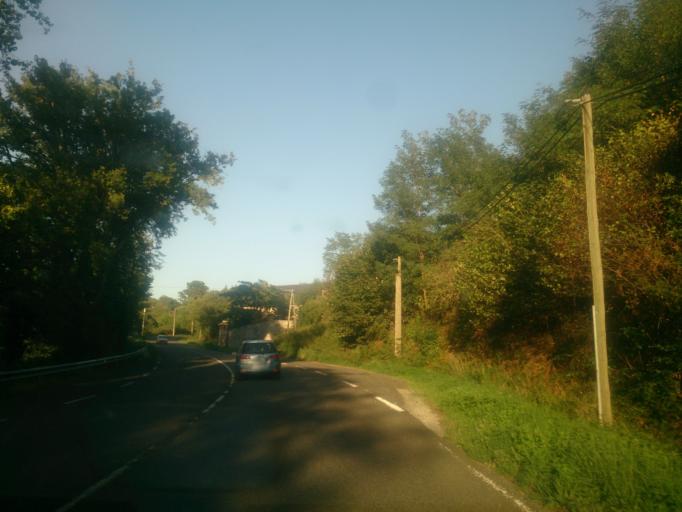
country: FR
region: Limousin
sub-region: Departement de la Correze
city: Brive-la-Gaillarde
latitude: 45.1405
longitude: 1.5204
